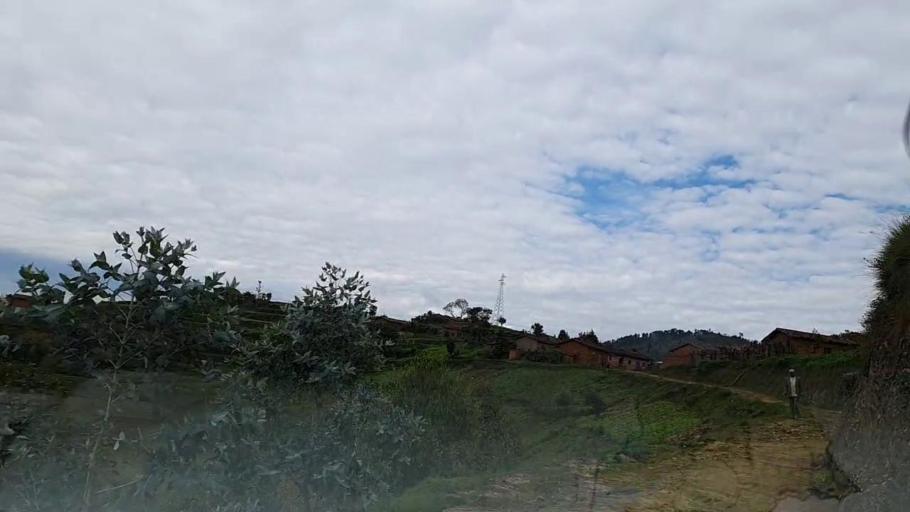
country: RW
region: Southern Province
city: Nzega
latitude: -2.4089
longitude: 29.4933
